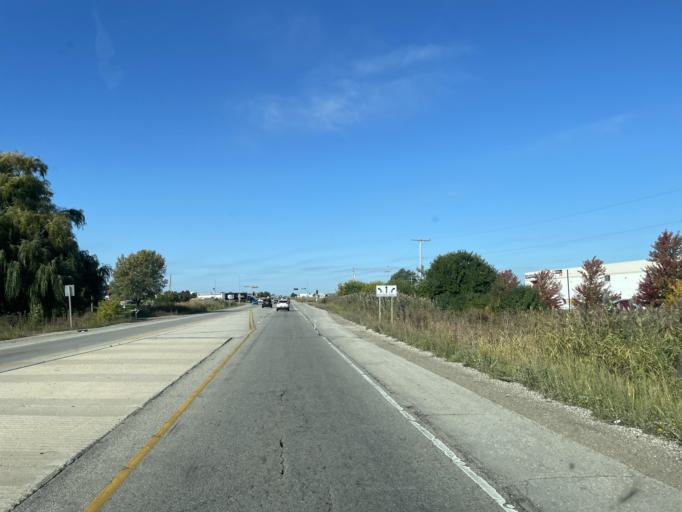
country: US
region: Wisconsin
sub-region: Kenosha County
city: Pleasant Prairie
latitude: 42.5891
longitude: -87.9124
